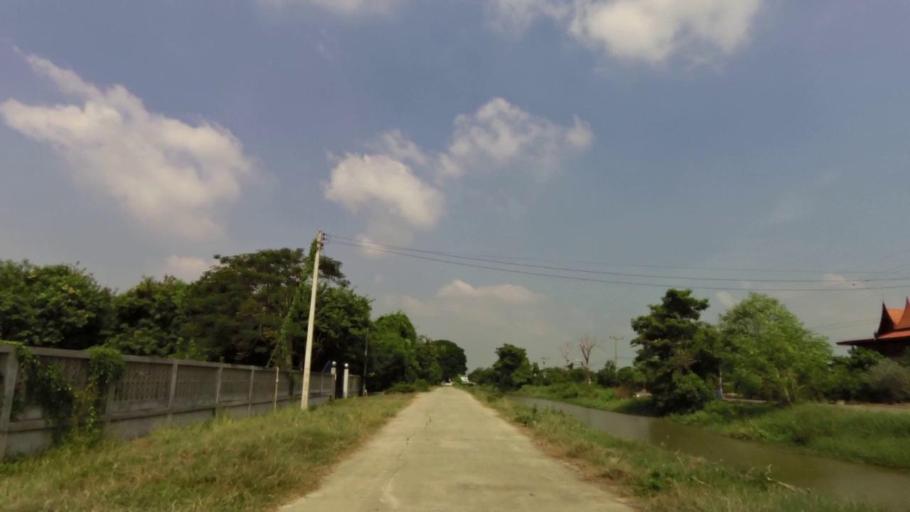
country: TH
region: Ang Thong
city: Ang Thong
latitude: 14.6061
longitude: 100.3992
